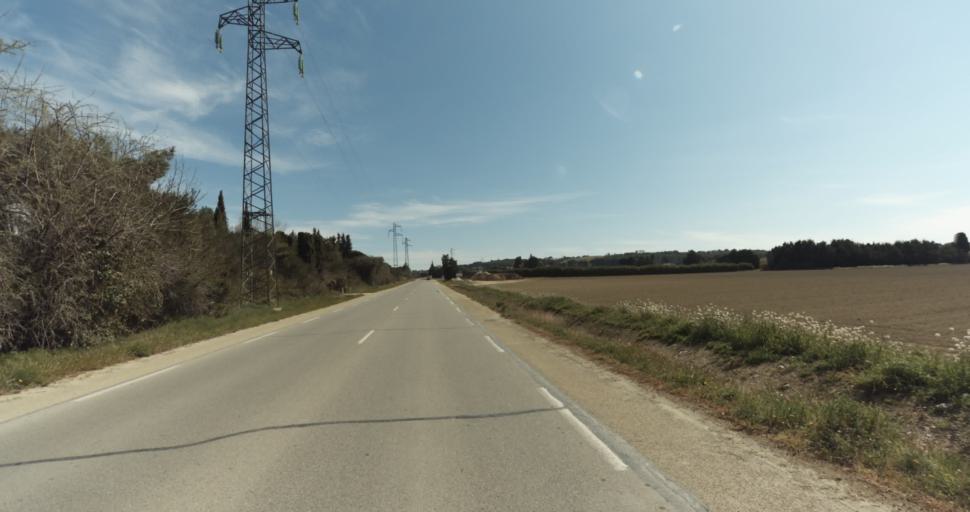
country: FR
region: Provence-Alpes-Cote d'Azur
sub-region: Departement des Bouches-du-Rhone
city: Lambesc
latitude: 43.6516
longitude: 5.2389
